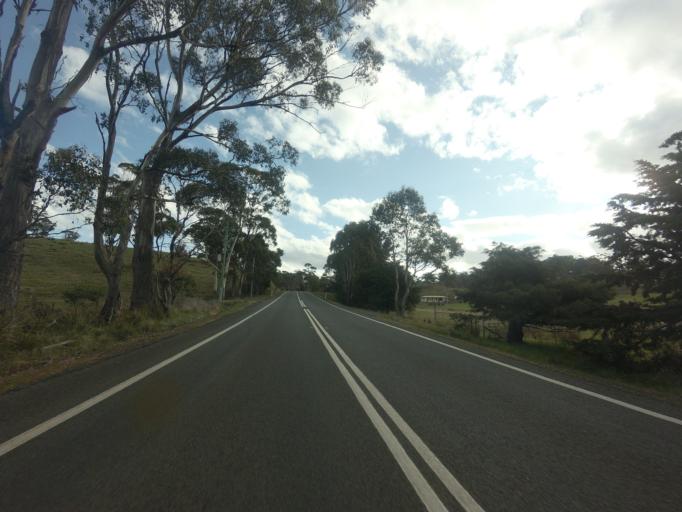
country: AU
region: Tasmania
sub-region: Sorell
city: Sorell
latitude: -42.6276
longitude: 147.6306
